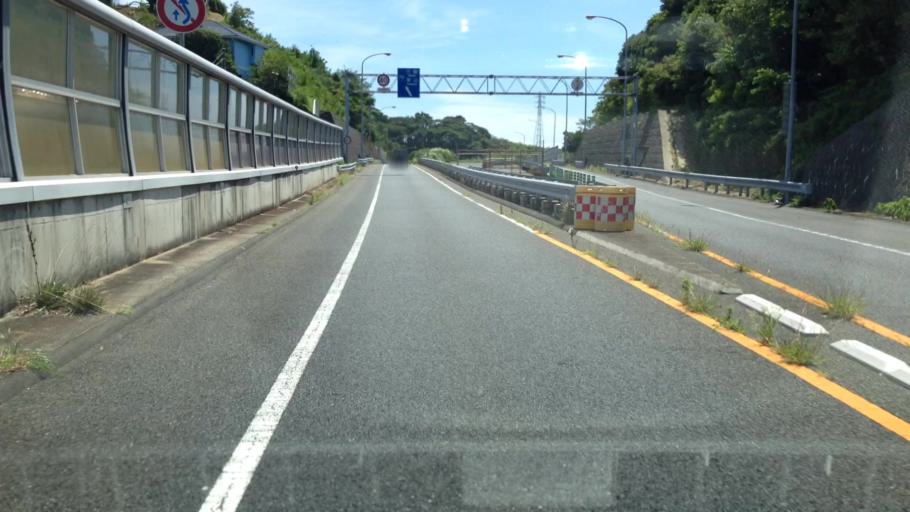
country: JP
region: Kanagawa
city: Yokosuka
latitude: 35.2157
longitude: 139.6374
